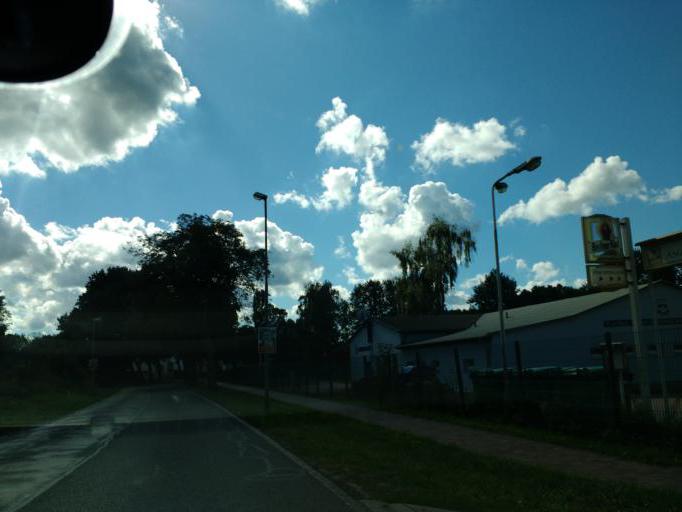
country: DE
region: Brandenburg
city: Mittenwalde
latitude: 52.2136
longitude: 13.5854
